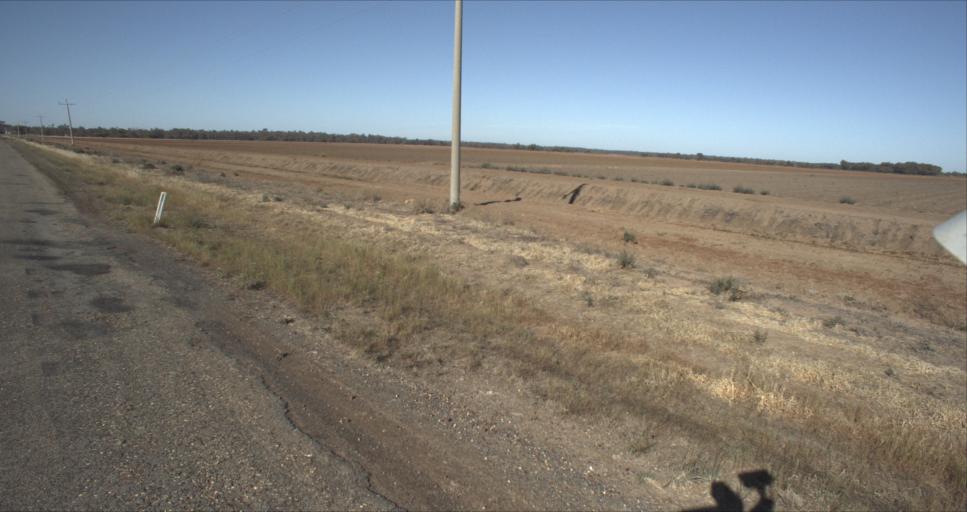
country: AU
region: New South Wales
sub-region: Leeton
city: Leeton
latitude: -34.5955
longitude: 146.2588
